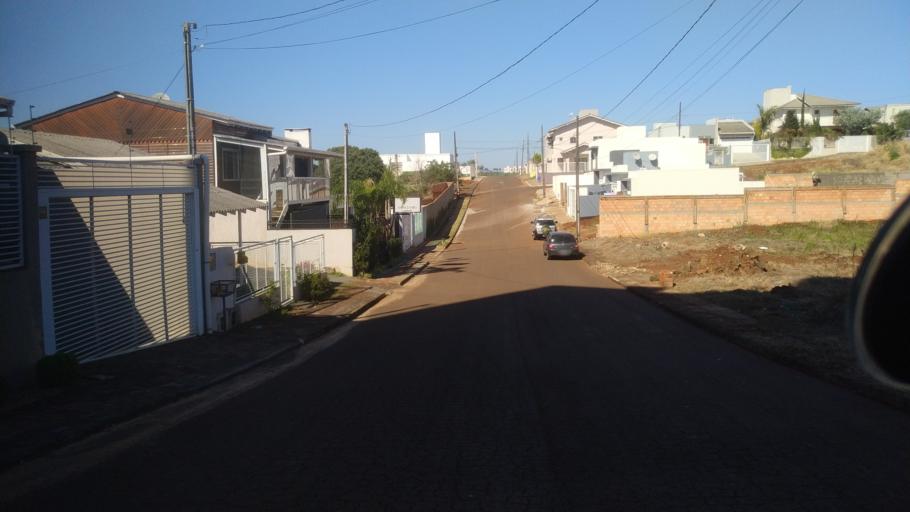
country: BR
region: Santa Catarina
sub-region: Chapeco
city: Chapeco
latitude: -27.0886
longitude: -52.5842
